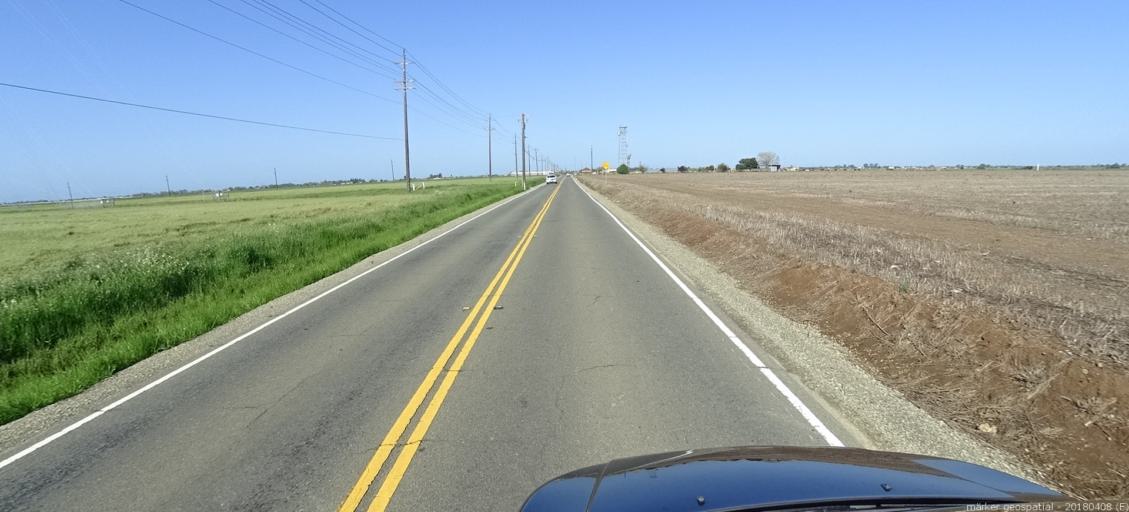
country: US
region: California
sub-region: Sacramento County
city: Elk Grove
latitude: 38.3726
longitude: -121.3768
